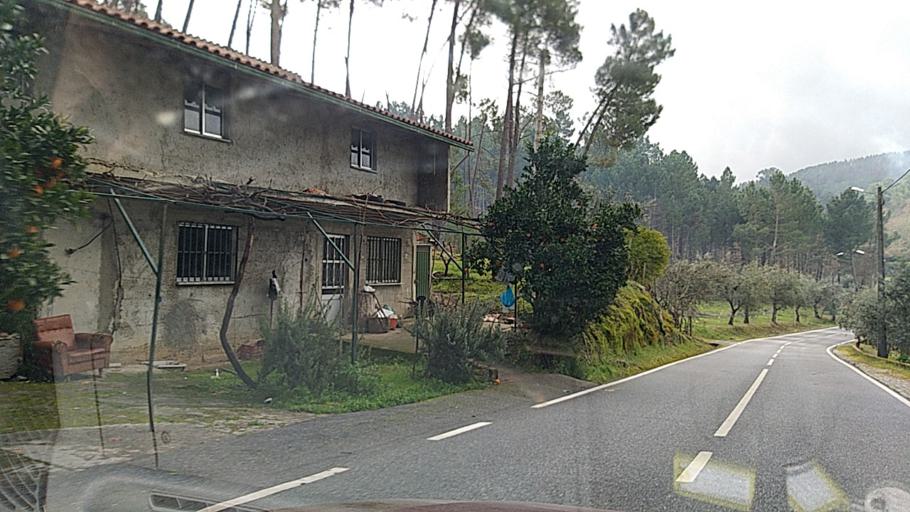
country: PT
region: Viseu
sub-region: Satao
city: Satao
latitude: 40.6583
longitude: -7.6543
